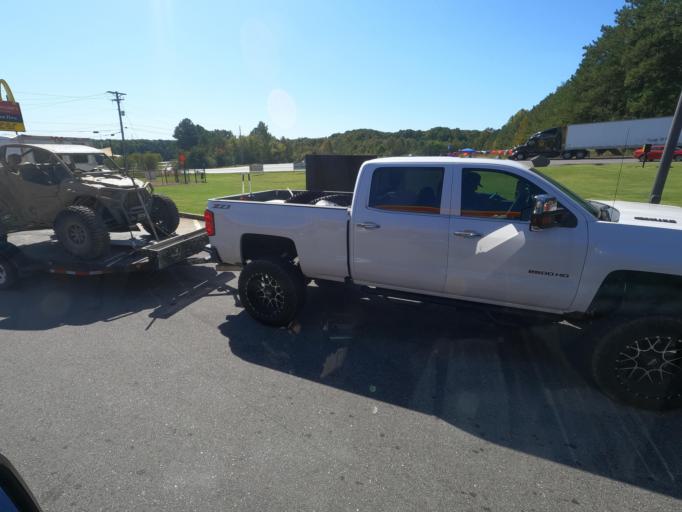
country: US
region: Tennessee
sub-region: Bradley County
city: Hopewell
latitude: 35.2904
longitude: -84.8178
